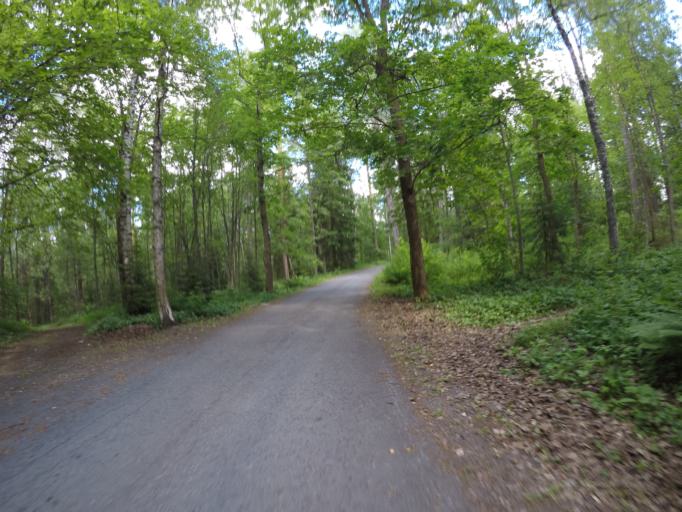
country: FI
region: Haeme
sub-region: Haemeenlinna
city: Haemeenlinna
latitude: 61.0115
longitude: 24.4488
